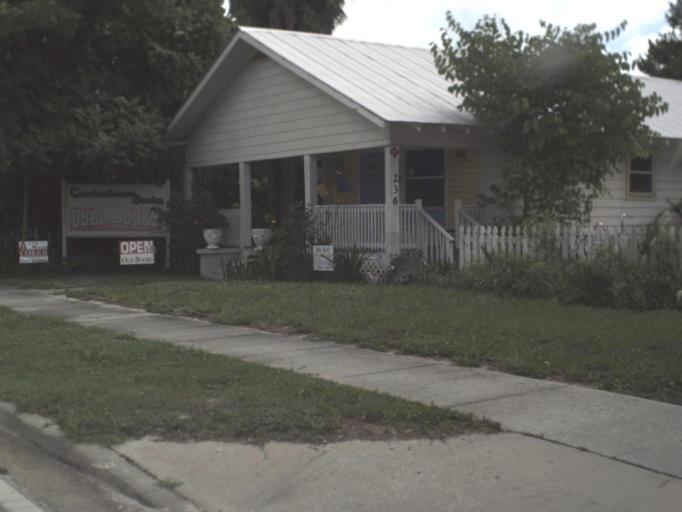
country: US
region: Florida
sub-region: DeSoto County
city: Arcadia
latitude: 27.2190
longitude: -81.8572
